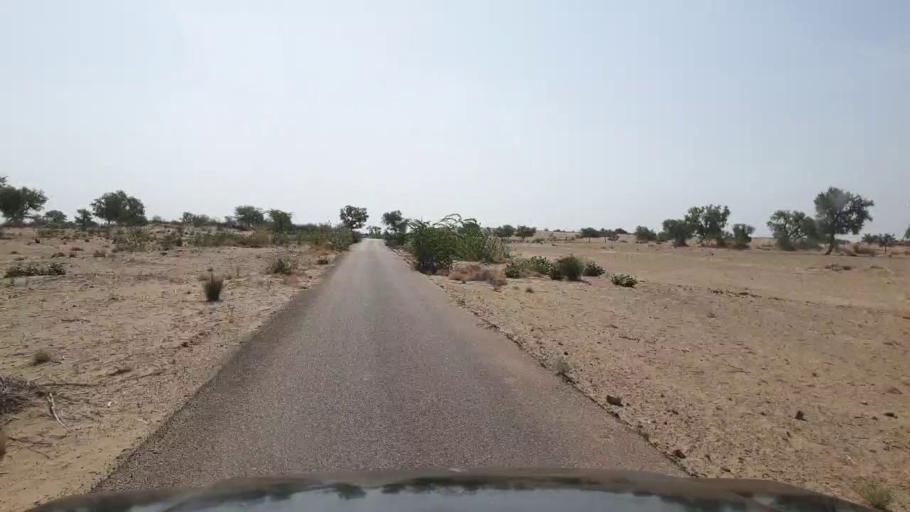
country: PK
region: Sindh
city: Islamkot
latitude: 24.9210
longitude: 70.1393
